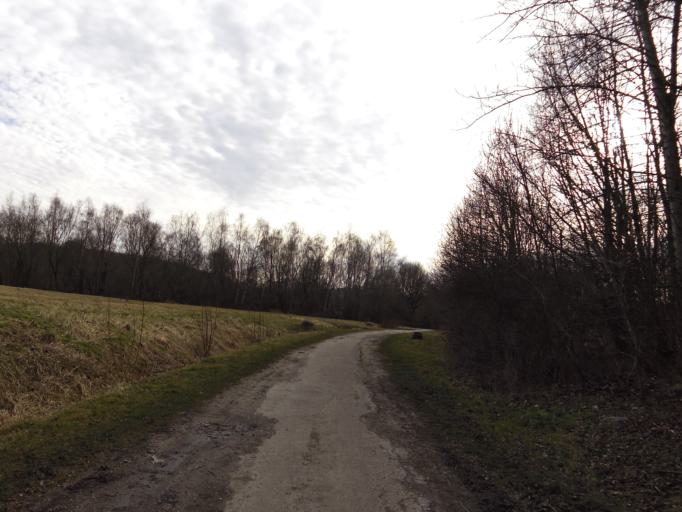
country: NL
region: Limburg
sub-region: Gemeente Kerkrade
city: Kerkrade
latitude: 50.8925
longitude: 6.0357
